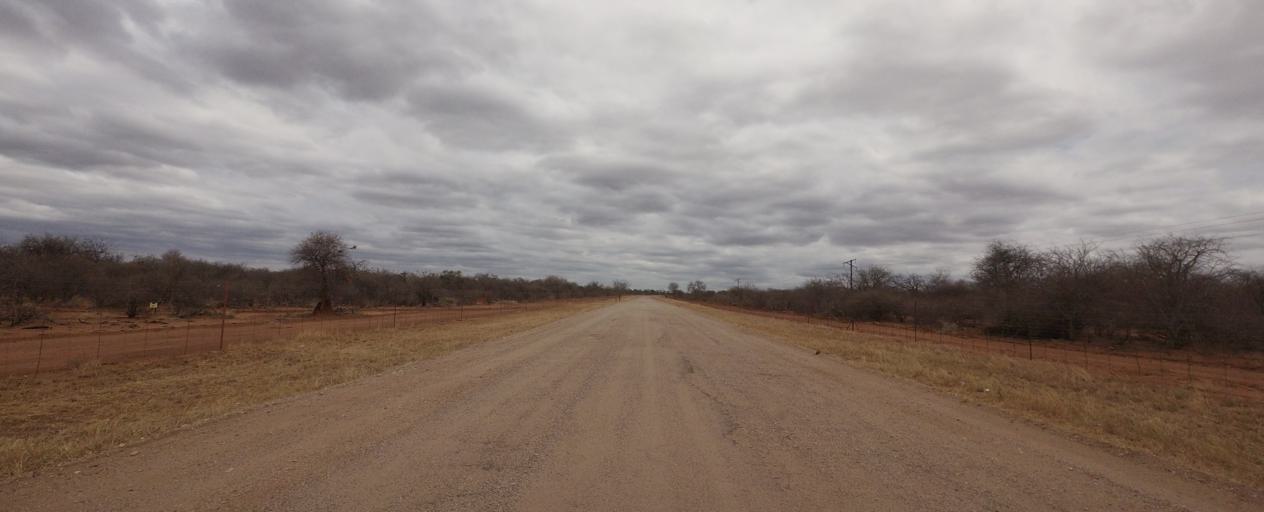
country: BW
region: Central
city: Mathathane
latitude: -22.7010
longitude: 28.6153
